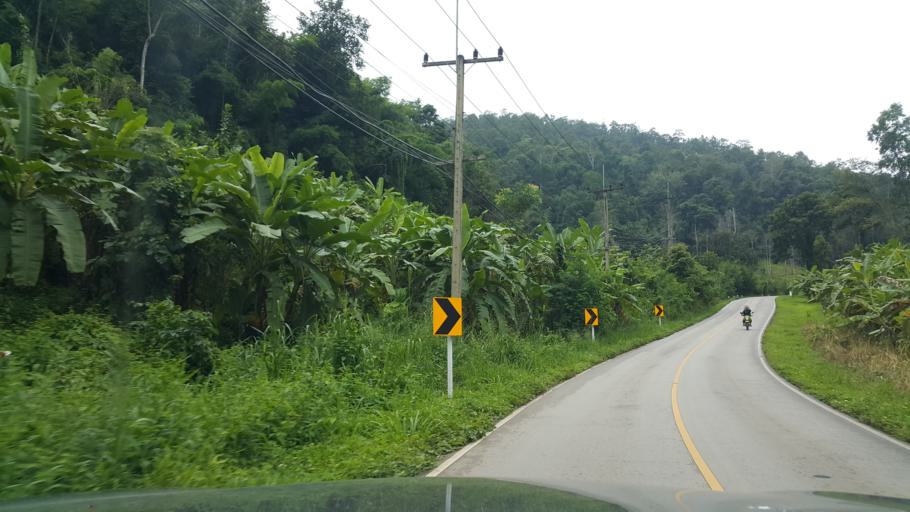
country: TH
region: Chiang Mai
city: Samoeng
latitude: 18.8662
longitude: 98.7177
